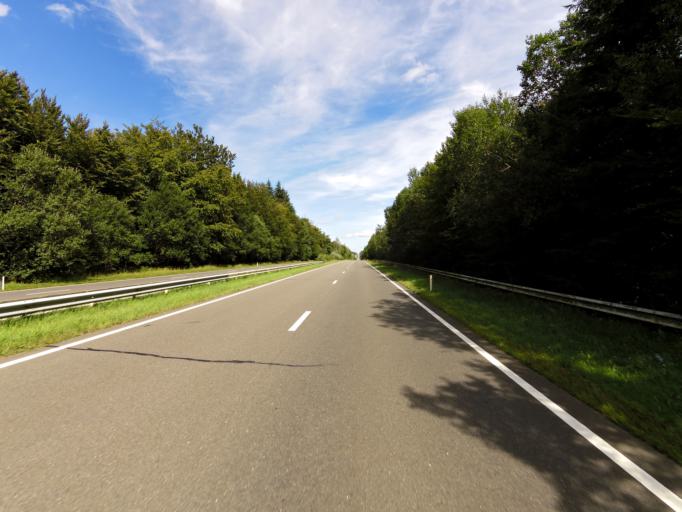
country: BE
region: Wallonia
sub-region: Province du Luxembourg
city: Saint-Hubert
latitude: 50.0764
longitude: 5.4323
